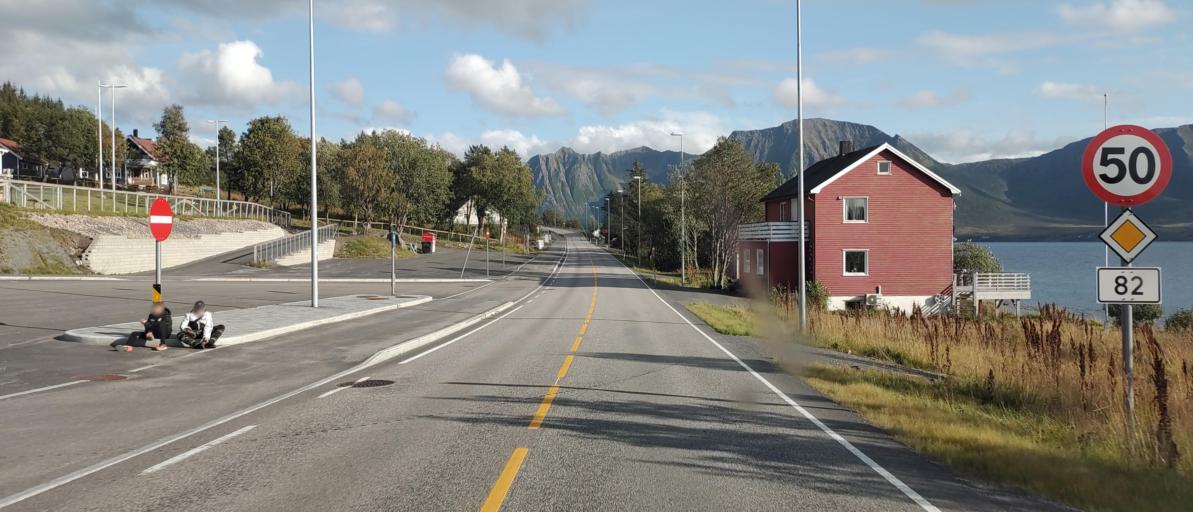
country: NO
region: Nordland
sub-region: Sortland
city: Sortland
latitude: 68.7536
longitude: 15.4693
